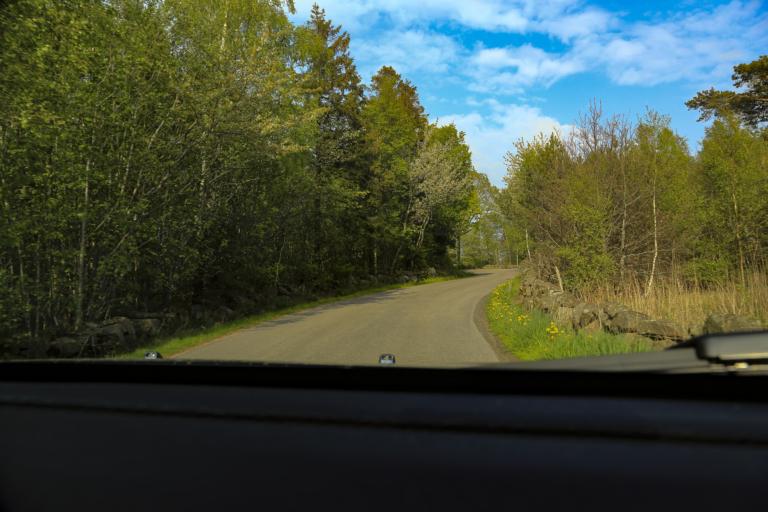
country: SE
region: Halland
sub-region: Varbergs Kommun
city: Traslovslage
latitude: 57.0892
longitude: 12.3229
